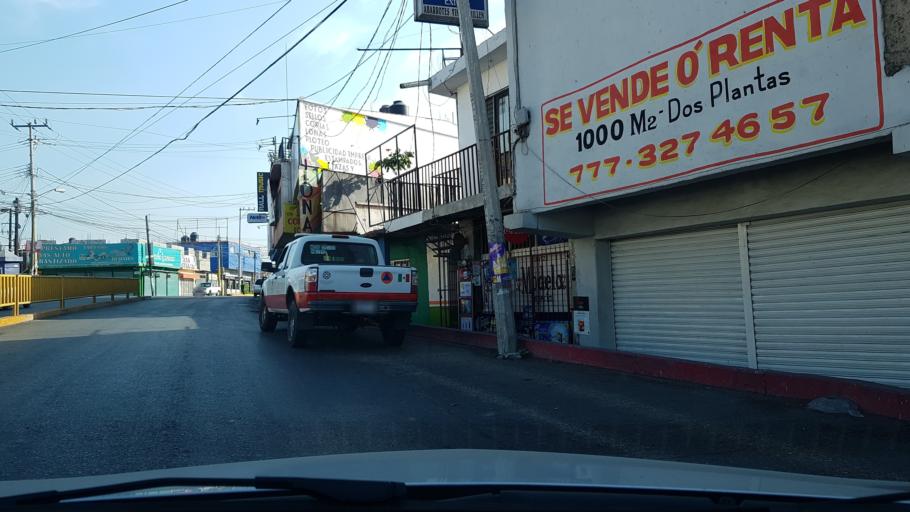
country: MX
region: Morelos
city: Temixco
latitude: 18.8453
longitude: -99.2238
